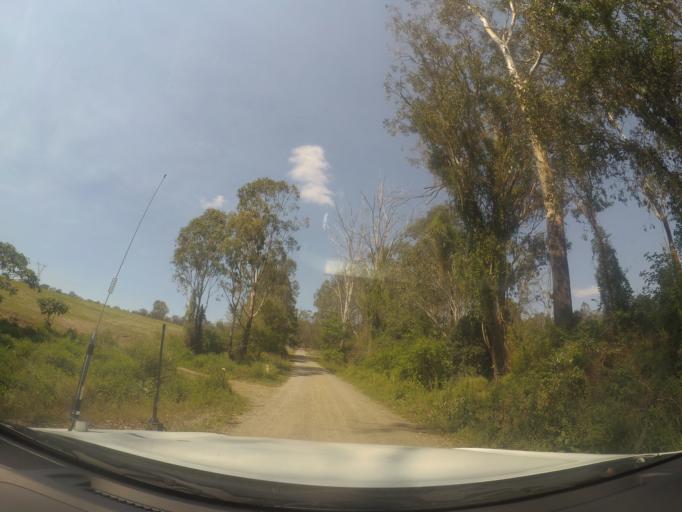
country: AU
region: Queensland
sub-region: Logan
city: North Maclean
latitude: -27.7726
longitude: 153.0385
